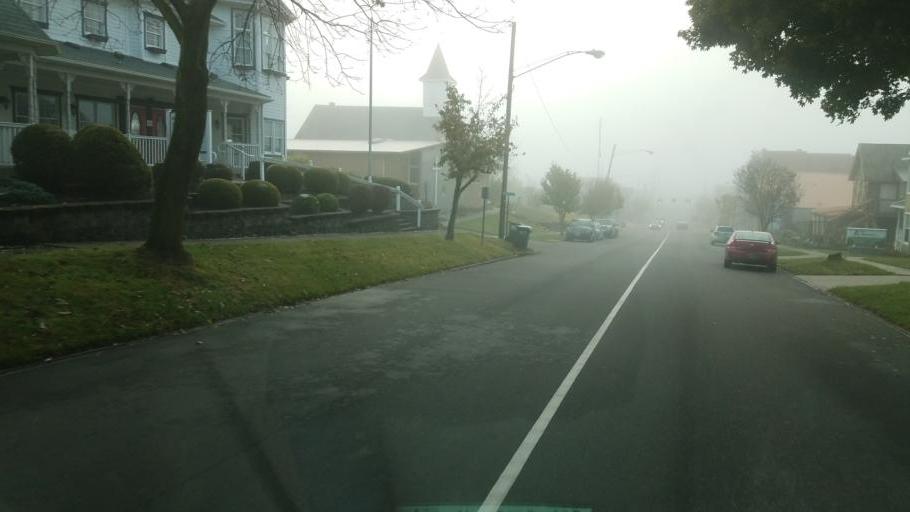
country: US
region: Ohio
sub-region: Tuscarawas County
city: Sugarcreek
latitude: 40.5038
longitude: -81.6422
